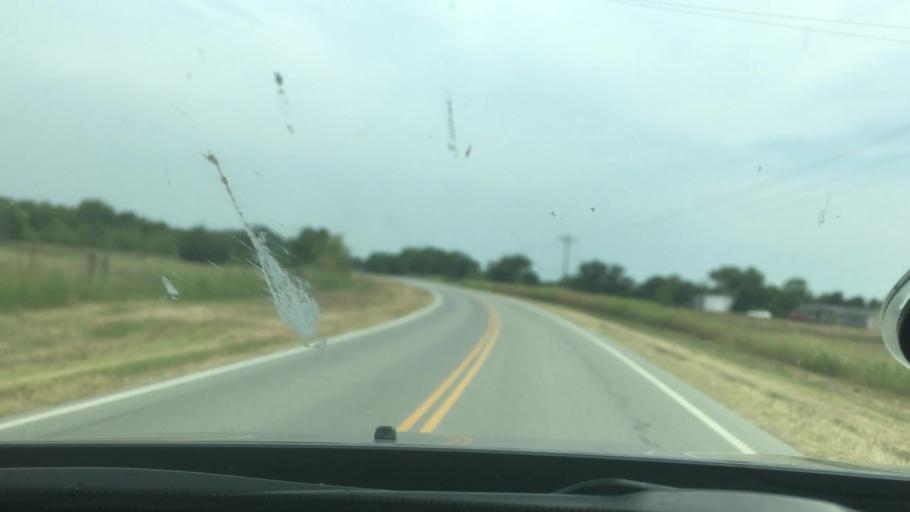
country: US
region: Oklahoma
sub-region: Coal County
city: Coalgate
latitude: 34.5786
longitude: -96.4077
